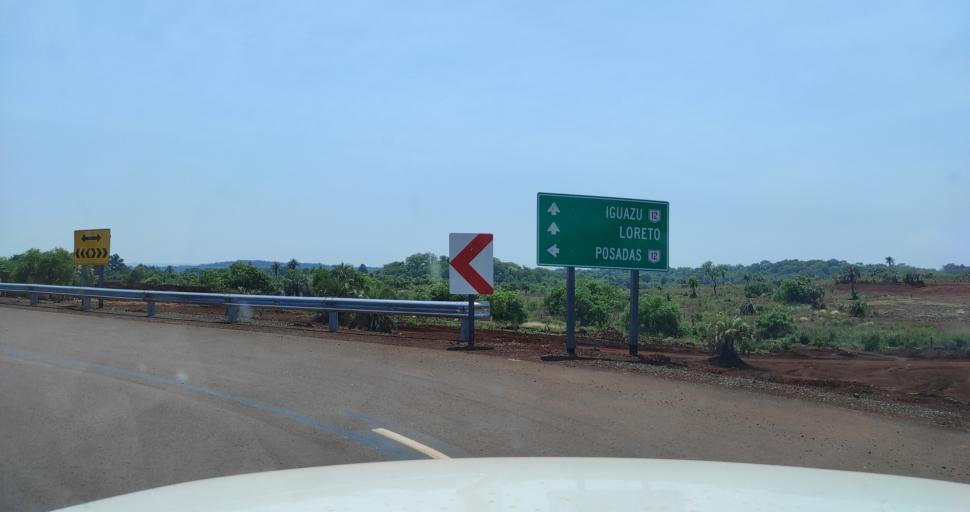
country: AR
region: Misiones
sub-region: Departamento de Candelaria
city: Loreto
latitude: -27.3388
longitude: -55.5428
